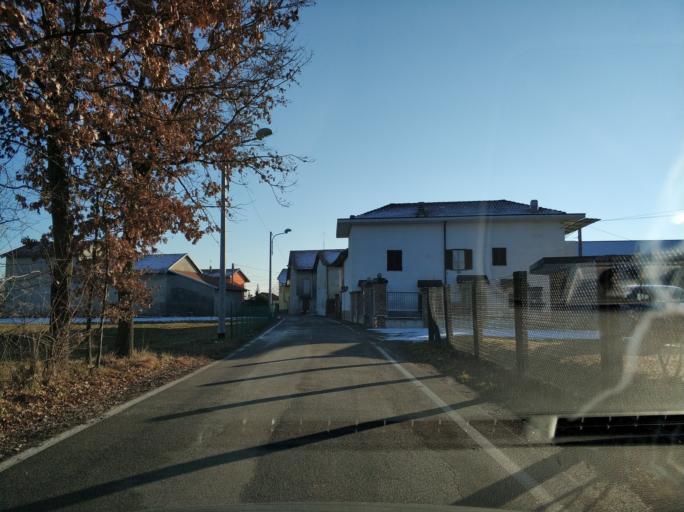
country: IT
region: Piedmont
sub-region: Provincia di Torino
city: San Francesco al Campo
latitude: 45.2352
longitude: 7.6554
